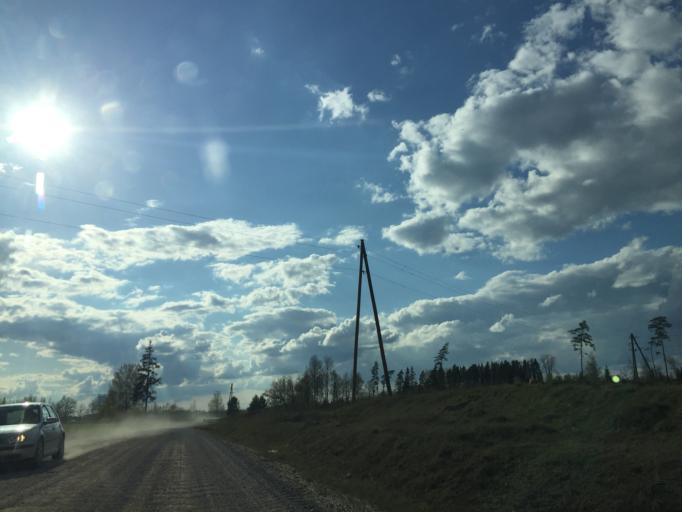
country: LV
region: Beverina
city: Murmuiza
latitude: 57.3985
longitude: 25.4796
